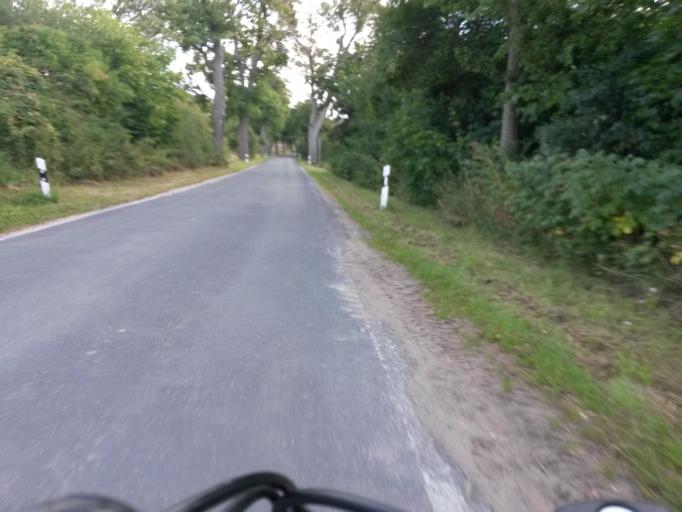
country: DE
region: Brandenburg
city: Althuttendorf
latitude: 53.0072
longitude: 13.8808
